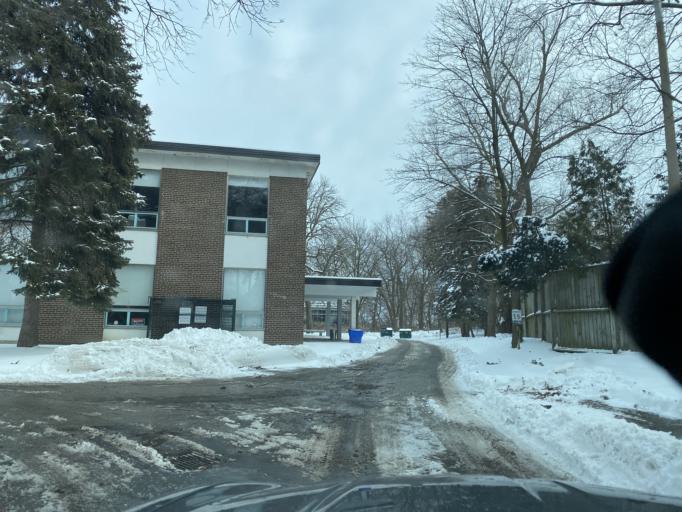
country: CA
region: Ontario
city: Toronto
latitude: 43.6735
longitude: -79.3666
